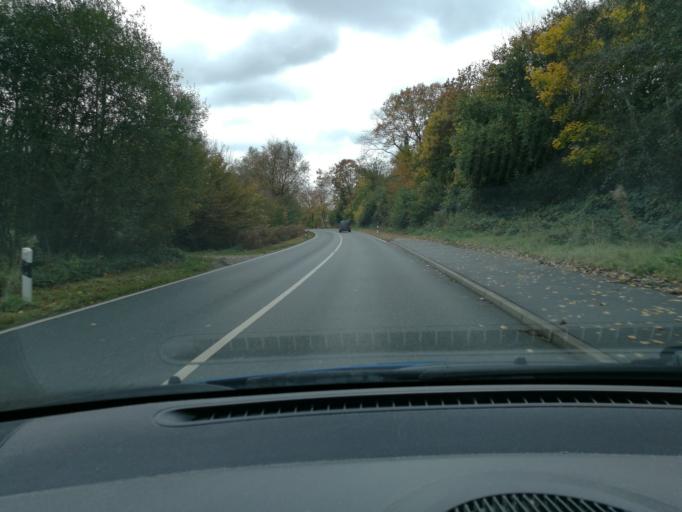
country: DE
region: Schleswig-Holstein
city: Pogeez
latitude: 53.7463
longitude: 10.7294
